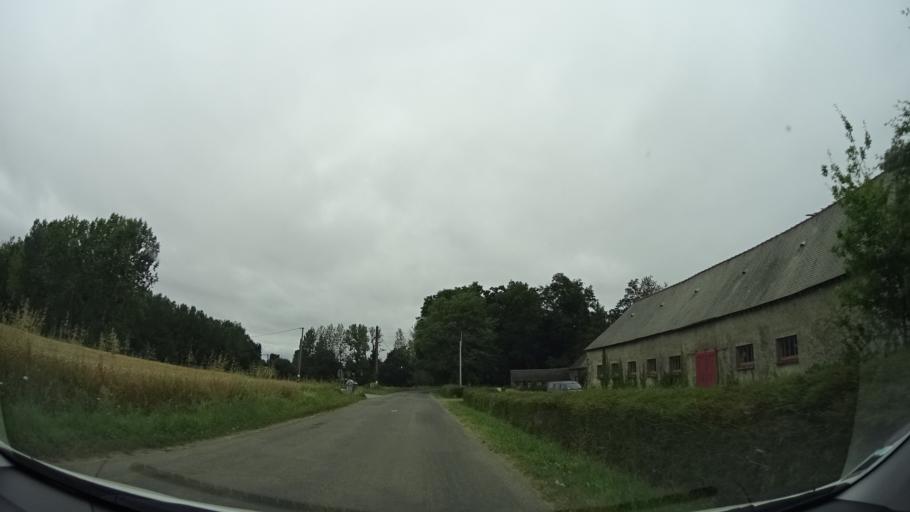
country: FR
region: Brittany
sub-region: Departement des Cotes-d'Armor
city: Evran
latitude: 48.3292
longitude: -1.9319
